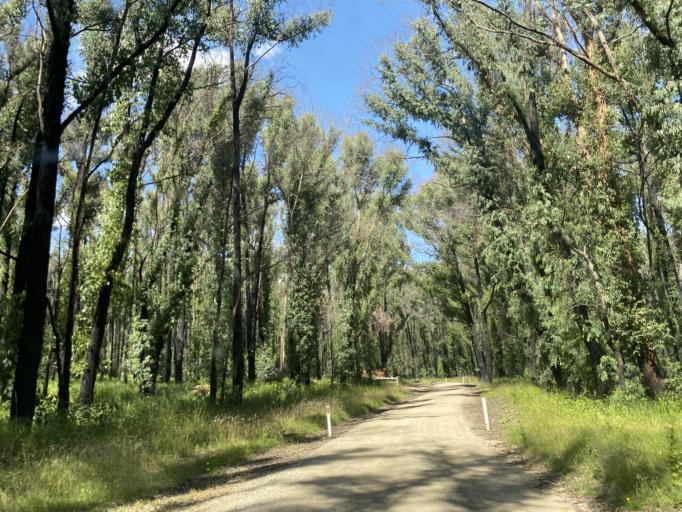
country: AU
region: Victoria
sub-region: Cardinia
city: Gembrook
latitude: -37.9832
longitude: 145.6448
